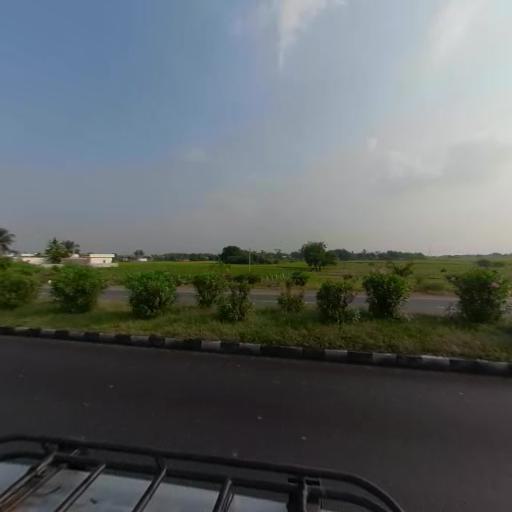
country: IN
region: Telangana
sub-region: Nalgonda
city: Suriapet
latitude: 17.1702
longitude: 79.5044
